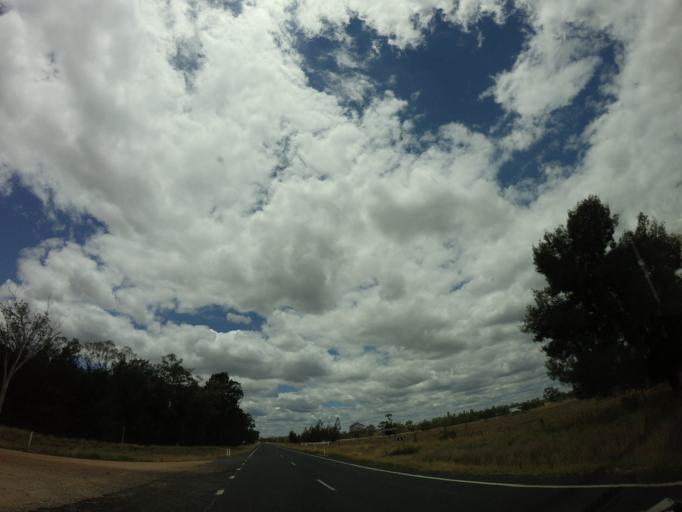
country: AU
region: Queensland
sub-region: Goondiwindi
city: Goondiwindi
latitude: -28.1597
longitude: 150.6411
